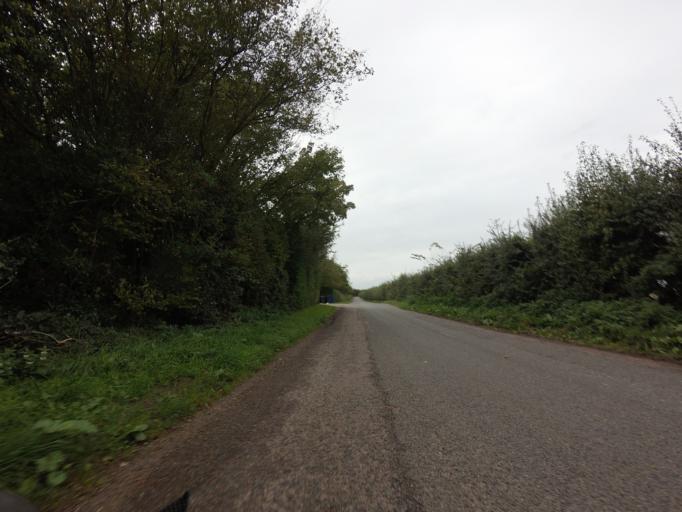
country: GB
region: England
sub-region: Cambridgeshire
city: Duxford
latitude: 52.0669
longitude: 0.1031
